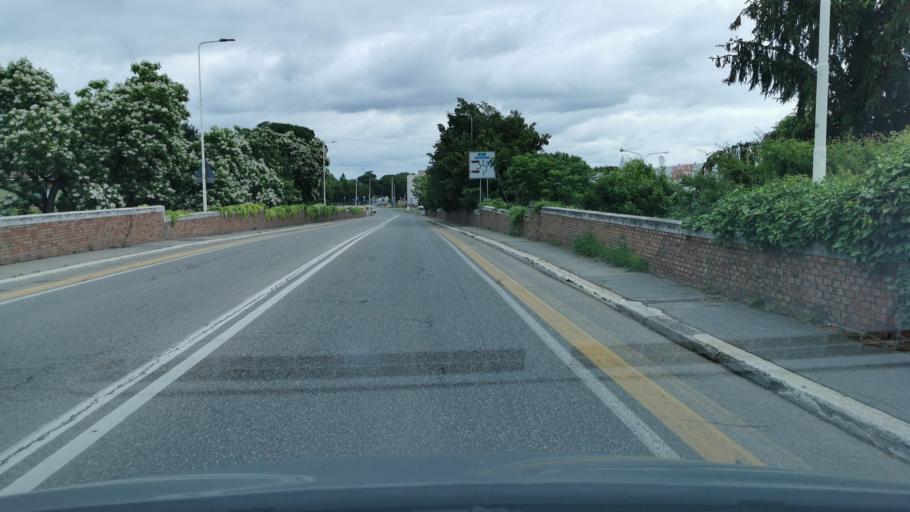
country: IT
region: Emilia-Romagna
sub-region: Provincia di Ravenna
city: Faenza
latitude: 44.2938
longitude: 11.8872
